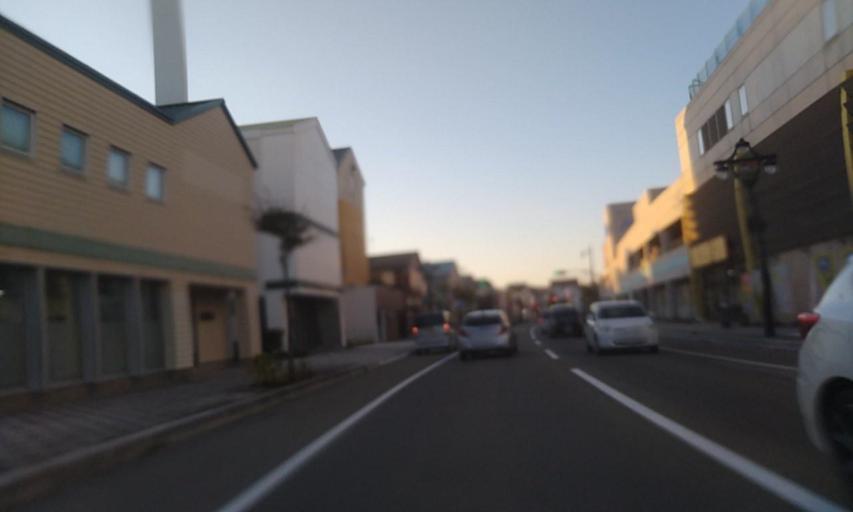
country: JP
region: Hokkaido
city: Shizunai-furukawacho
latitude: 42.1612
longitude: 142.7759
